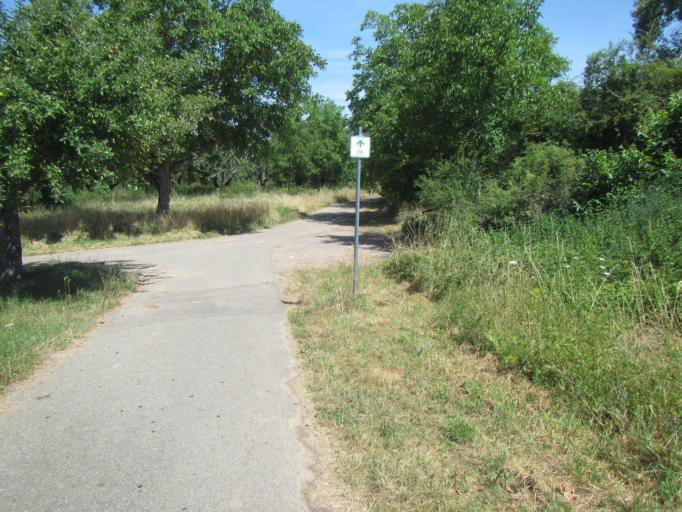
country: DE
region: Rheinland-Pfalz
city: Ilbesheim
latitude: 49.1920
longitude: 8.0585
